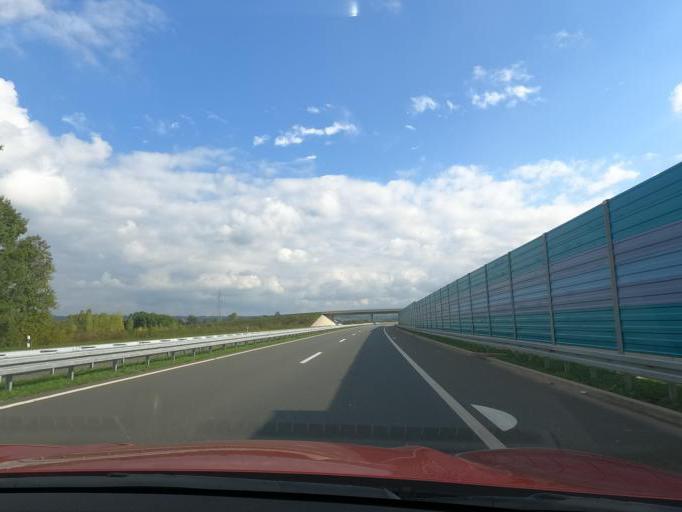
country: RS
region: Central Serbia
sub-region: Kolubarski Okrug
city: Ljig
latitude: 44.2863
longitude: 20.2505
